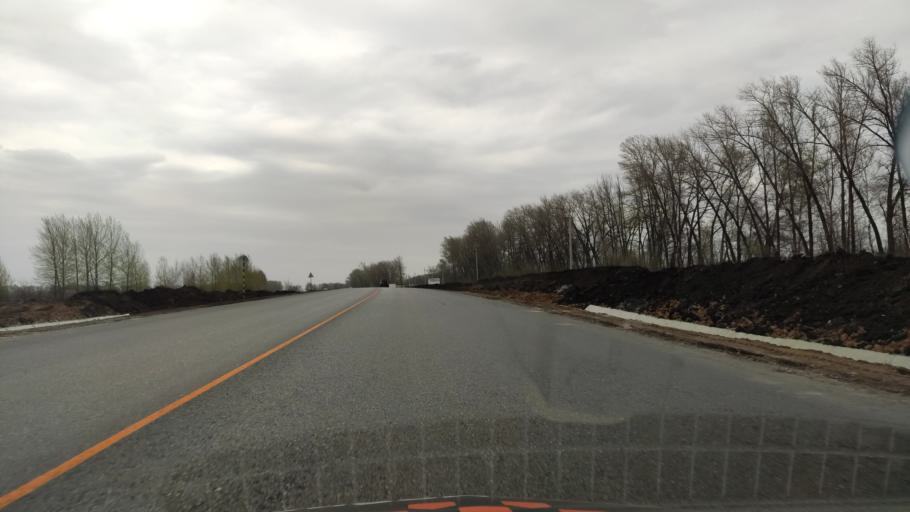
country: RU
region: Kursk
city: Gorshechnoye
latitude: 51.5483
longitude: 38.0536
